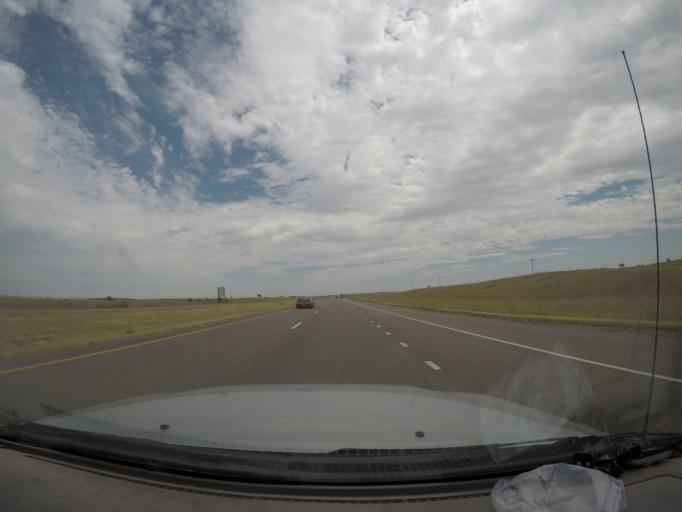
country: US
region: Nebraska
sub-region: Kimball County
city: Kimball
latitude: 41.2170
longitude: -103.6568
